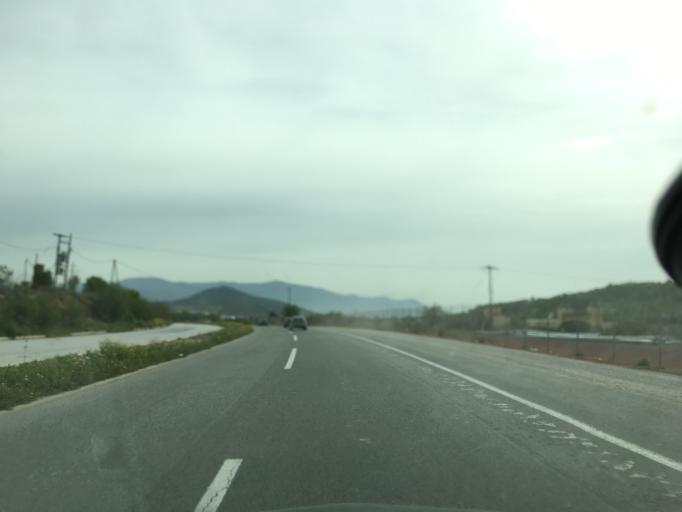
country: GR
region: Thessaly
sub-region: Nomos Magnisias
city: Velestino
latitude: 39.3838
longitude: 22.8402
